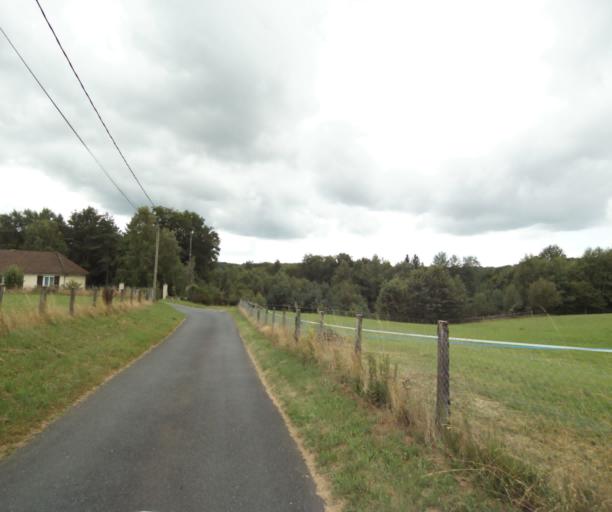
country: FR
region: Limousin
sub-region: Departement de la Correze
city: Sainte-Fortunade
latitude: 45.1826
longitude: 1.8127
